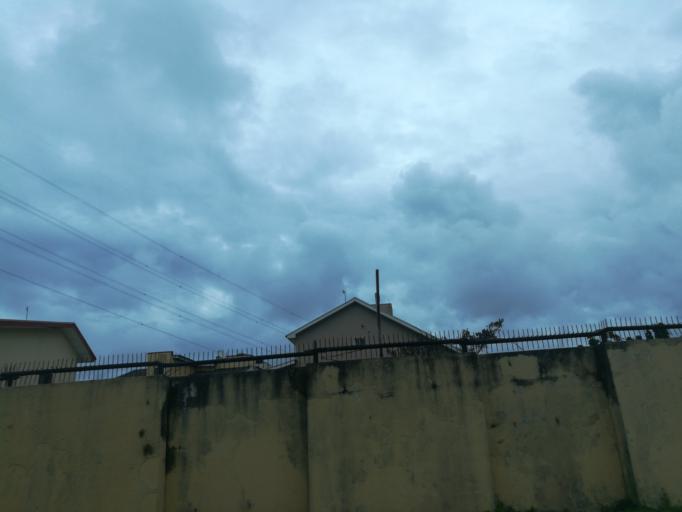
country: NG
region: Lagos
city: Ikoyi
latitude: 6.4456
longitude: 3.4548
